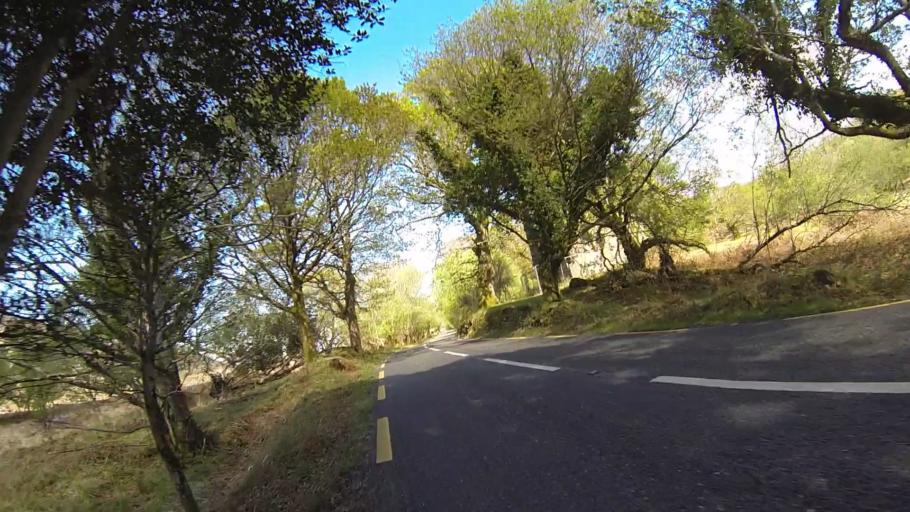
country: IE
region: Munster
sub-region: Ciarrai
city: Cill Airne
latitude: 51.9873
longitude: -9.5590
